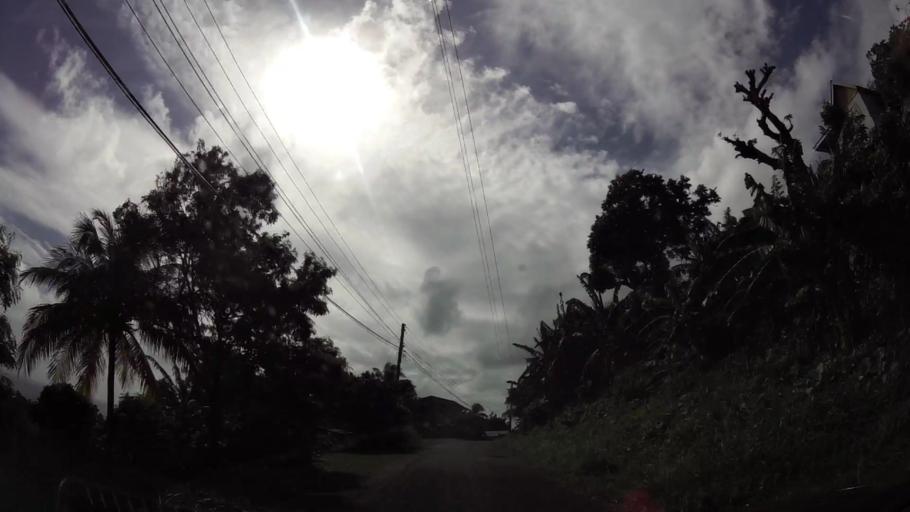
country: DM
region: Saint David
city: Castle Bruce
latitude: 15.4677
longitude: -61.2482
